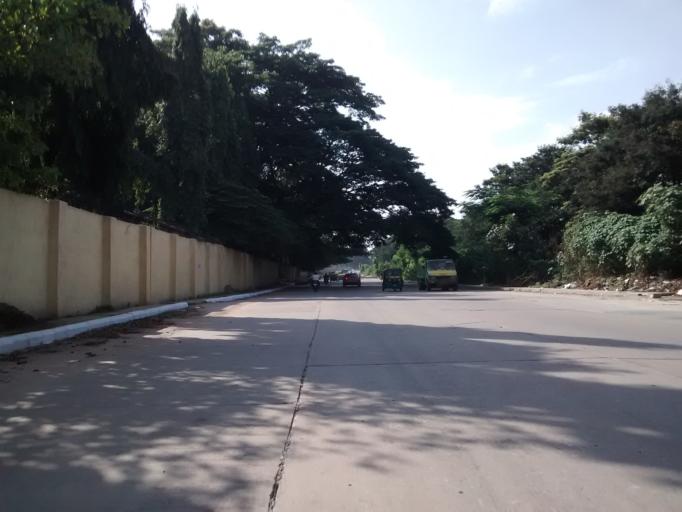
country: IN
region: Karnataka
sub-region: Bangalore Urban
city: Bangalore
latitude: 12.9776
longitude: 77.6540
